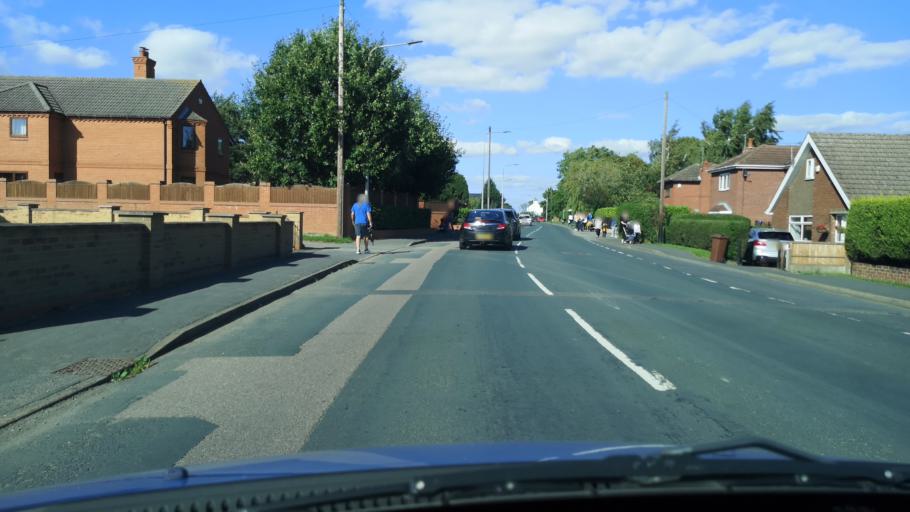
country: GB
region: England
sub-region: North Lincolnshire
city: Belton
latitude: 53.5526
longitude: -0.8168
